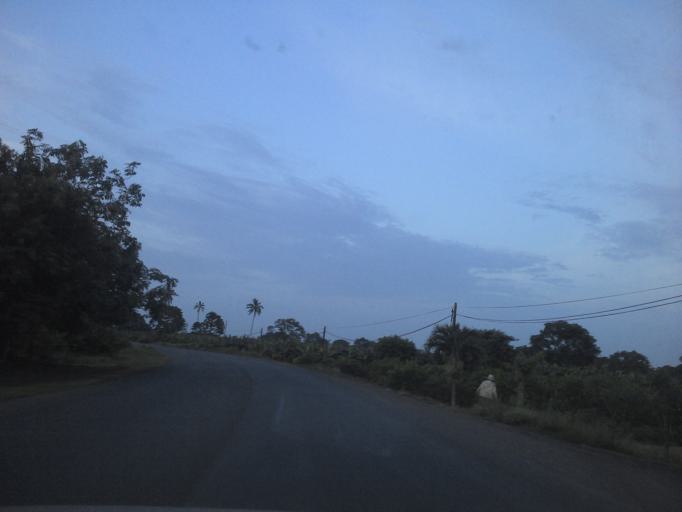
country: MX
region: Veracruz
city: San Rafael
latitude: 20.1822
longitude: -96.8357
